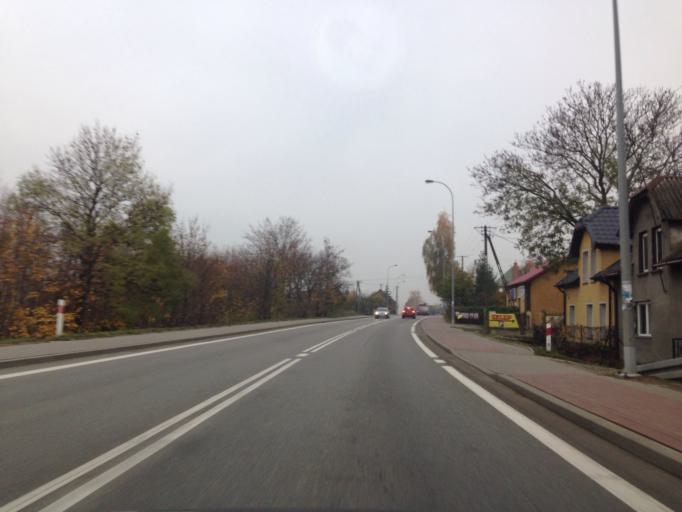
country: PL
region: Pomeranian Voivodeship
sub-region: Powiat gdanski
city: Pszczolki
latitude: 54.1891
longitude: 18.6751
